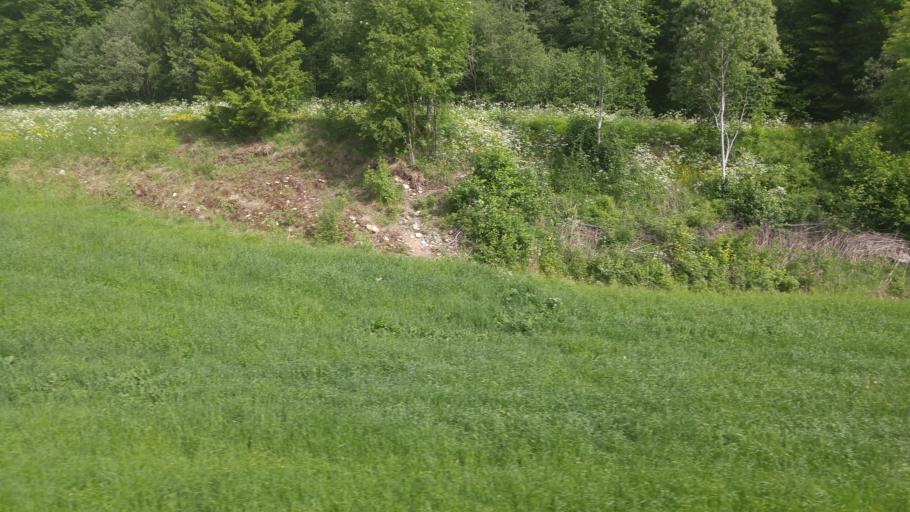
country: NO
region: Sor-Trondelag
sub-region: Midtre Gauldal
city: Storen
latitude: 63.0195
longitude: 10.4152
